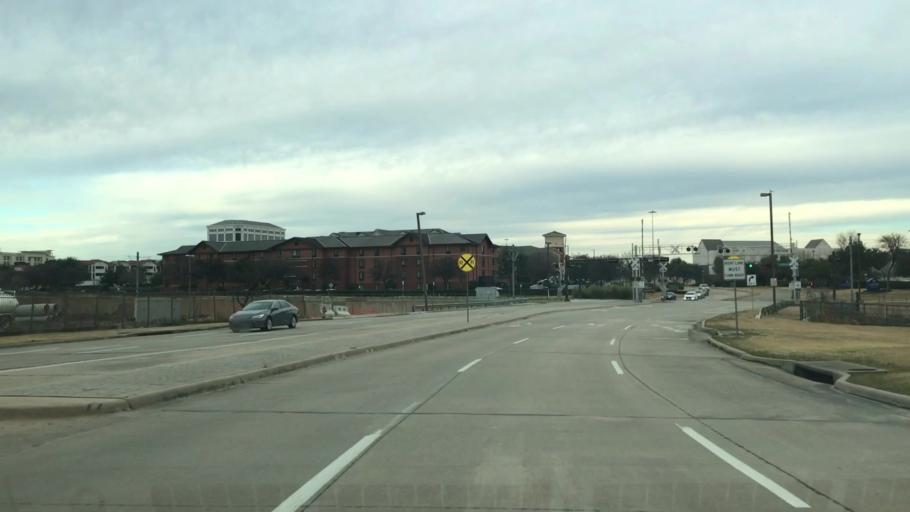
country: US
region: Texas
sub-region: Dallas County
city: Irving
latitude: 32.8812
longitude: -96.9535
